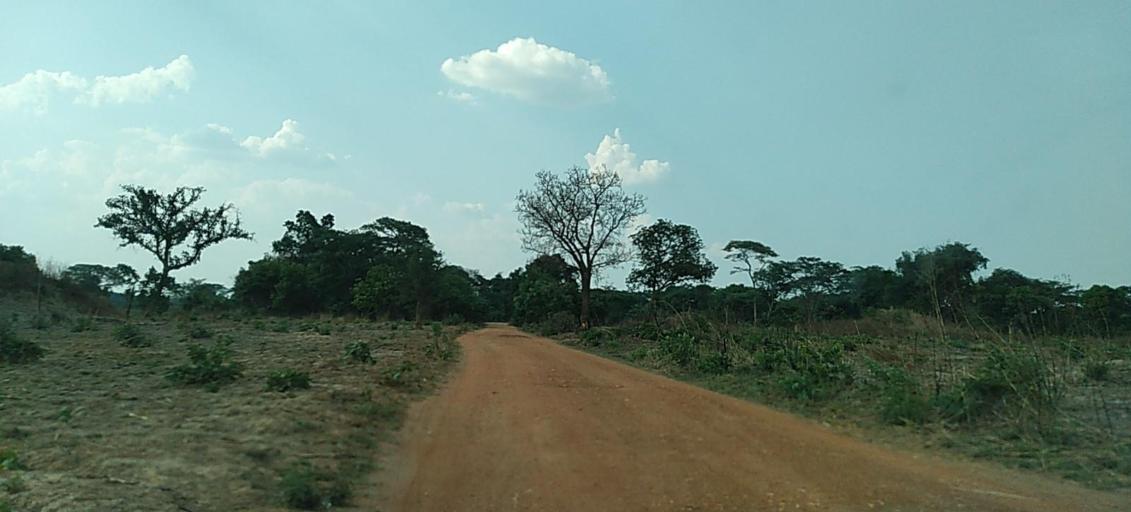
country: ZM
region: Copperbelt
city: Mpongwe
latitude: -13.4900
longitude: 28.0847
